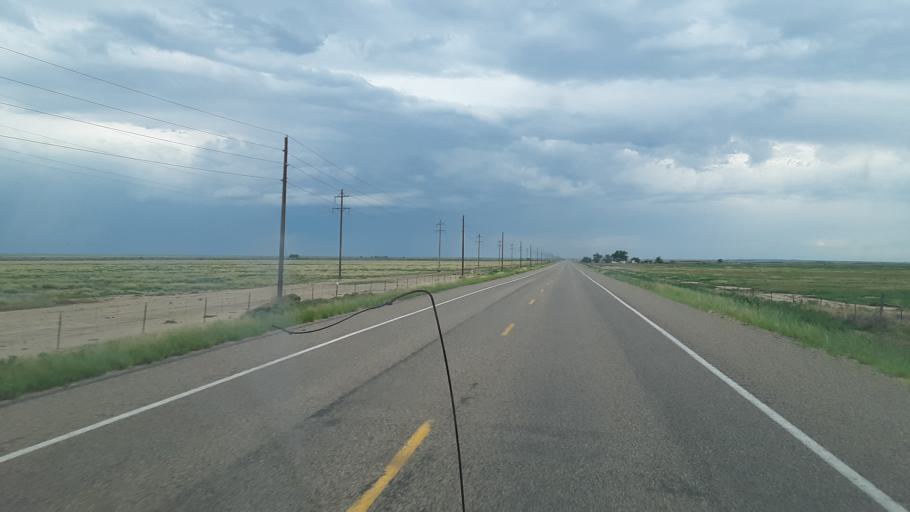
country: US
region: Colorado
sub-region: Crowley County
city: Ordway
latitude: 38.1963
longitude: -103.7481
